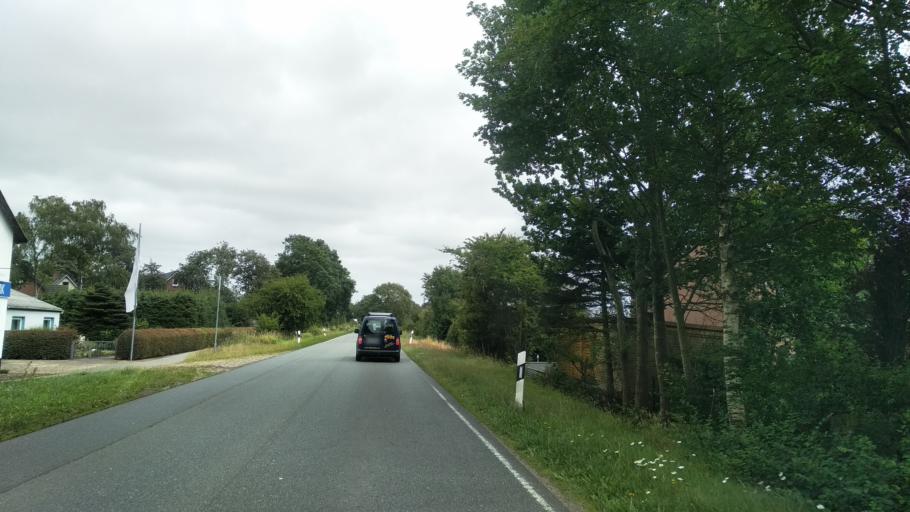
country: DE
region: Schleswig-Holstein
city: Jarplund-Weding
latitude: 54.7381
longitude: 9.4362
